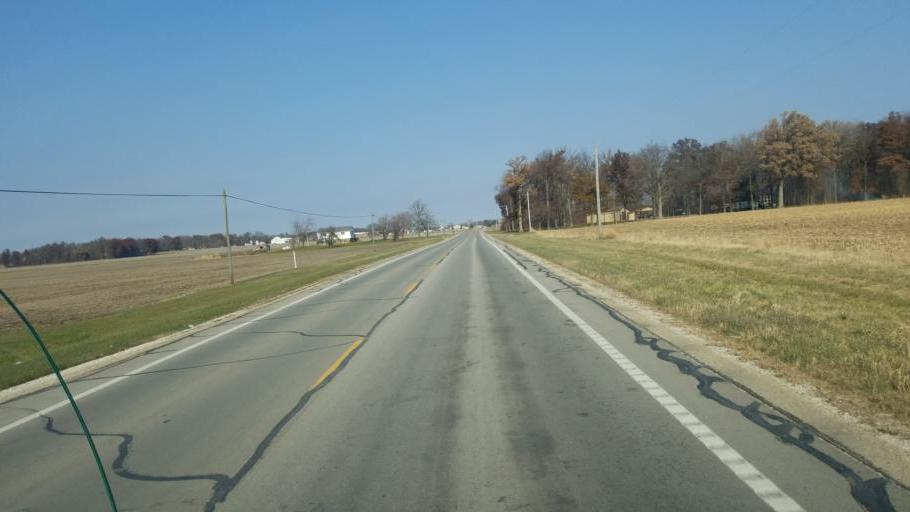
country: US
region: Ohio
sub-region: Mercer County
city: Coldwater
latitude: 40.5348
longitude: -84.6286
